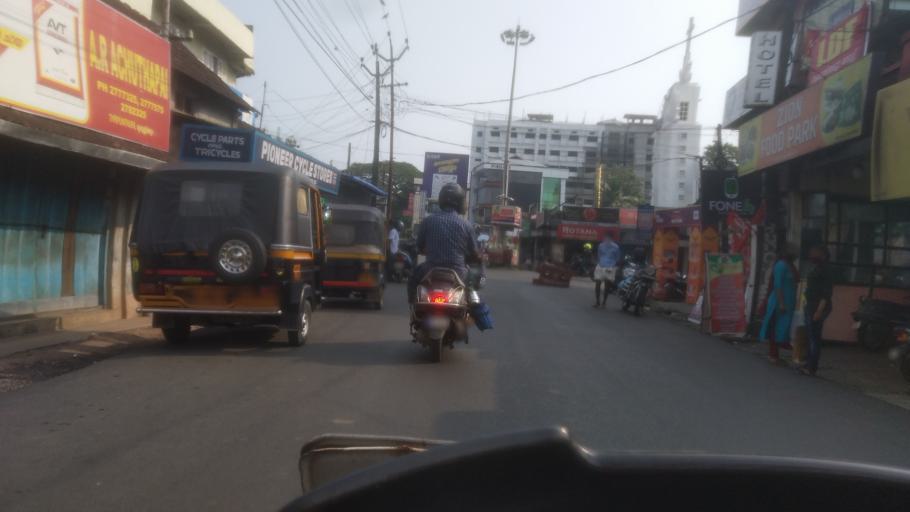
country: IN
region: Kerala
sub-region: Alappuzha
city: Arukutti
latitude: 9.9453
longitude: 76.3488
